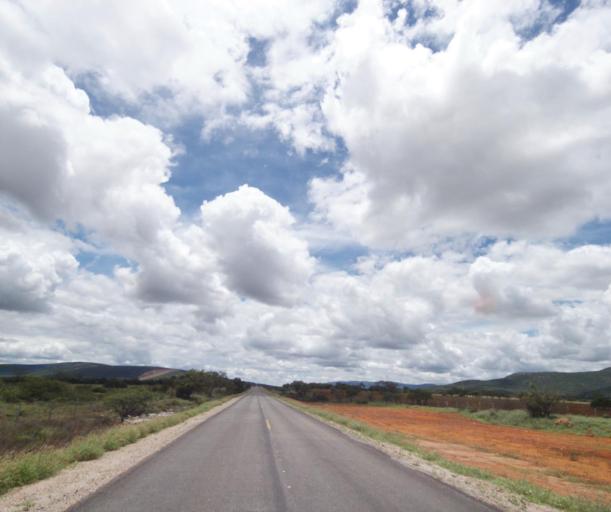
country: BR
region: Bahia
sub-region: Brumado
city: Brumado
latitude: -14.1608
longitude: -41.5289
